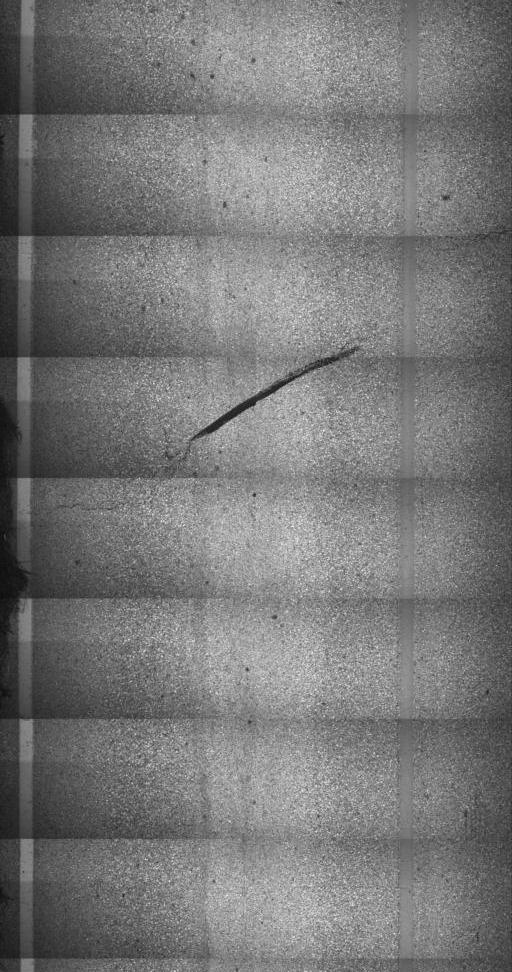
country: US
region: New York
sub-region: Washington County
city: Granville
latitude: 43.3530
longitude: -73.1529
